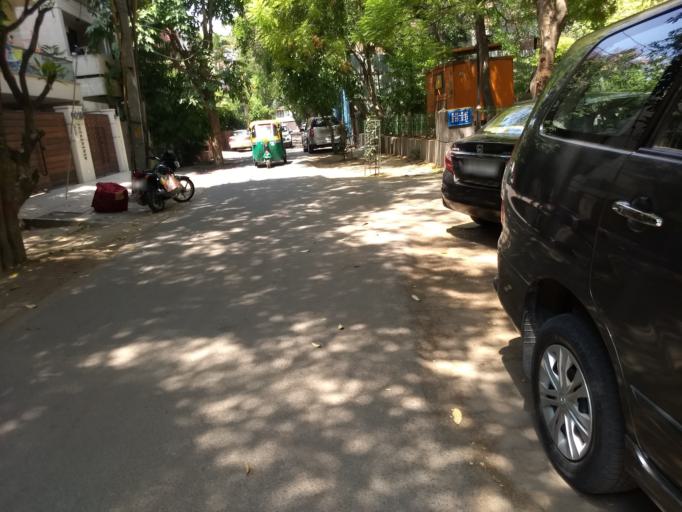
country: IN
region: NCT
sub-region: New Delhi
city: New Delhi
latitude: 28.5578
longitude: 77.2135
